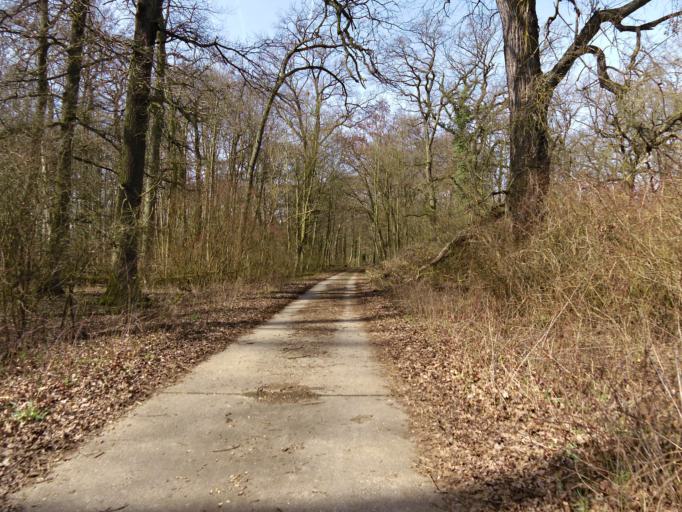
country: DE
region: Rheinland-Pfalz
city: Gimbsheim
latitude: 49.8065
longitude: 8.4061
